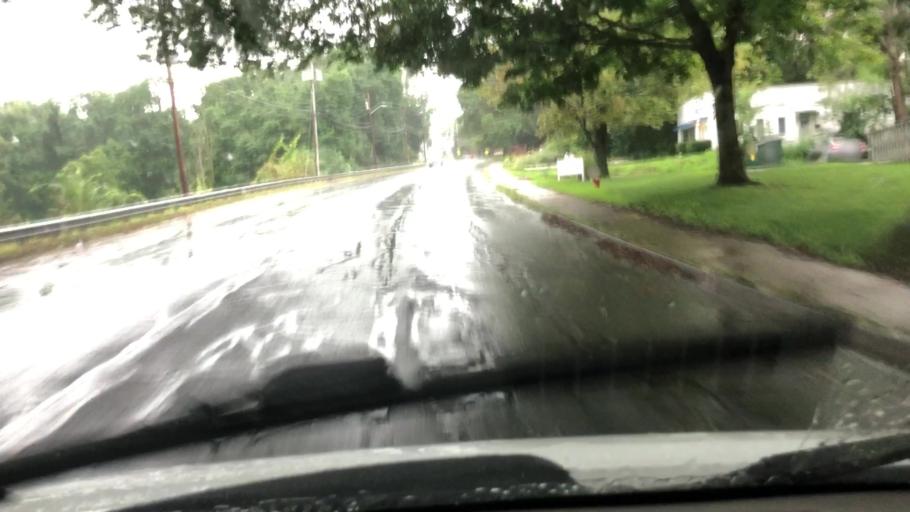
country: US
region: Massachusetts
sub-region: Hampshire County
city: Northampton
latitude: 42.3338
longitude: -72.6610
